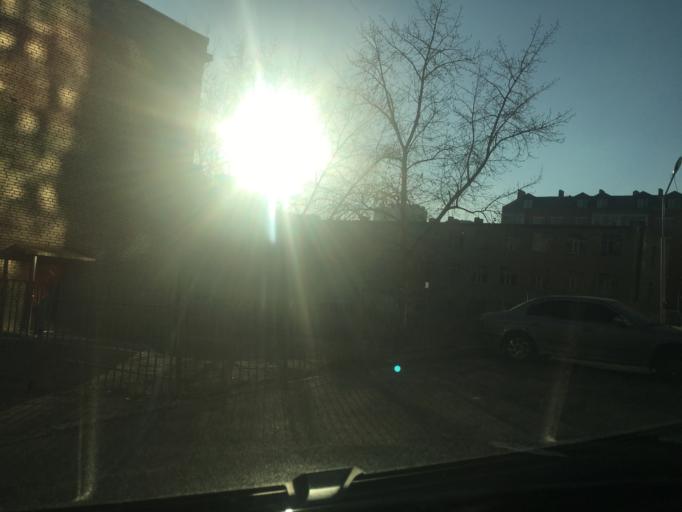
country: MN
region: Ulaanbaatar
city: Ulaanbaatar
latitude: 47.9168
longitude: 106.8793
